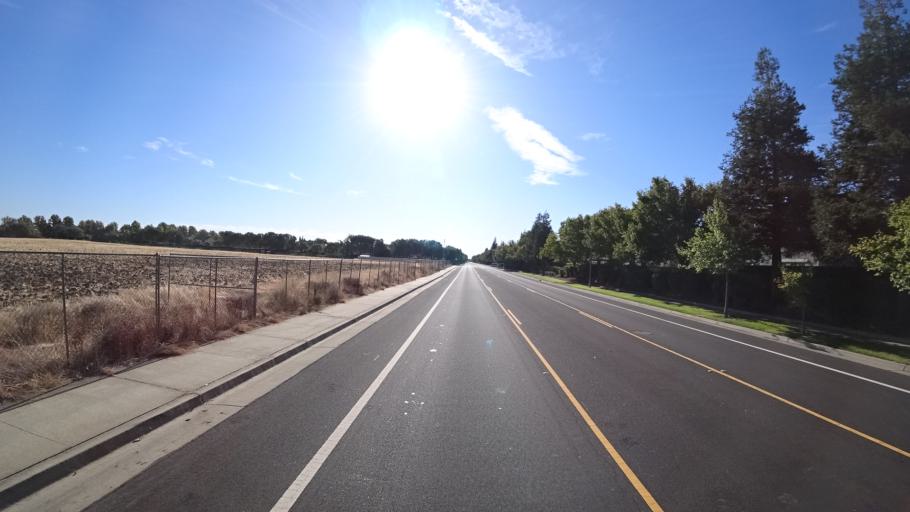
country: US
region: California
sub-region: Sacramento County
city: Laguna
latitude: 38.4060
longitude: -121.4775
